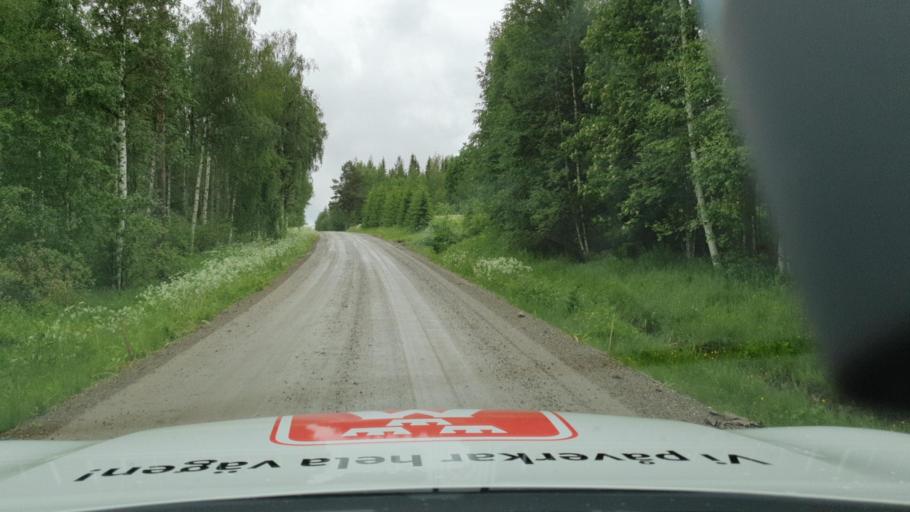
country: SE
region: Vaesterbotten
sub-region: Dorotea Kommun
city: Dorotea
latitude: 64.0122
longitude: 16.7981
